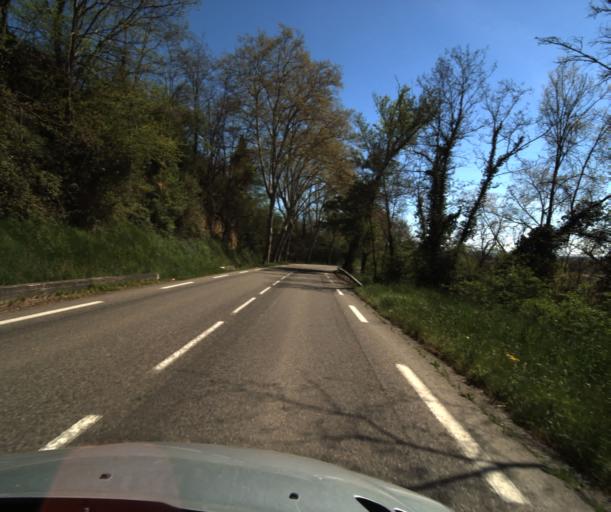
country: FR
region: Midi-Pyrenees
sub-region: Departement du Tarn-et-Garonne
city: Lafrancaise
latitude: 44.1239
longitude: 1.2394
